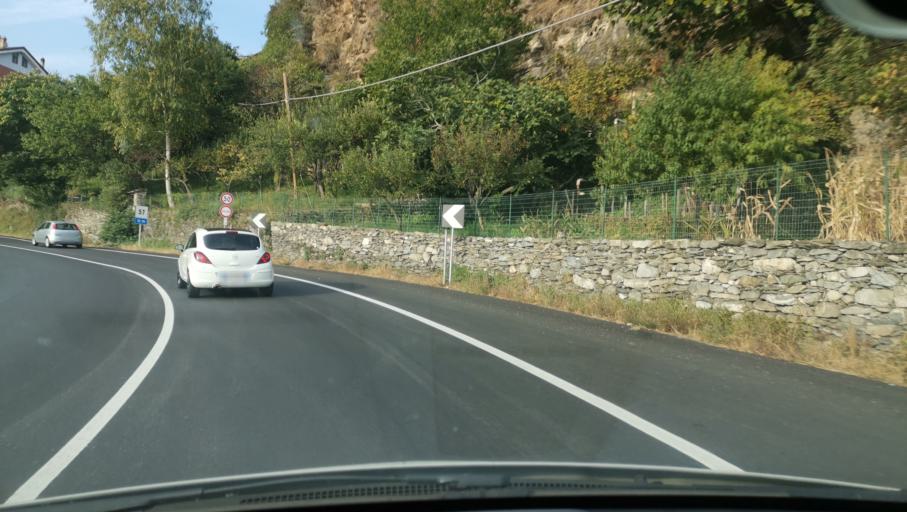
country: IT
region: Piedmont
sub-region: Provincia di Torino
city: San Giuseppe
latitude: 45.1334
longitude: 7.0402
